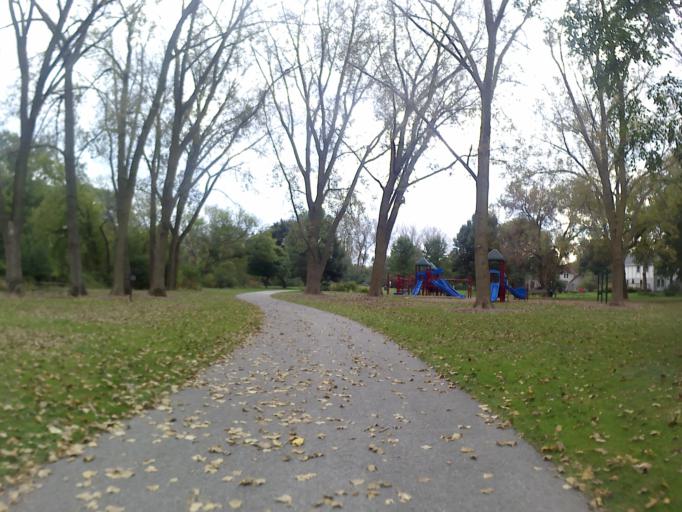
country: US
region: Illinois
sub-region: DuPage County
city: Naperville
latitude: 41.7737
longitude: -88.1670
